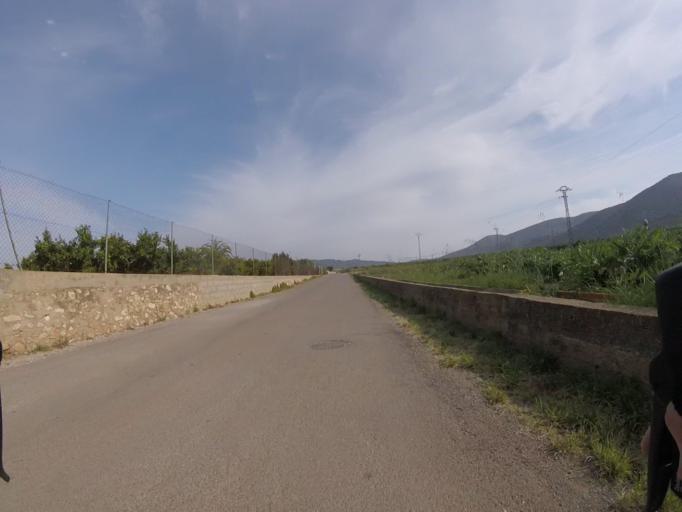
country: ES
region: Valencia
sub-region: Provincia de Castello
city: Alcoceber
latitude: 40.2607
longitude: 0.2530
